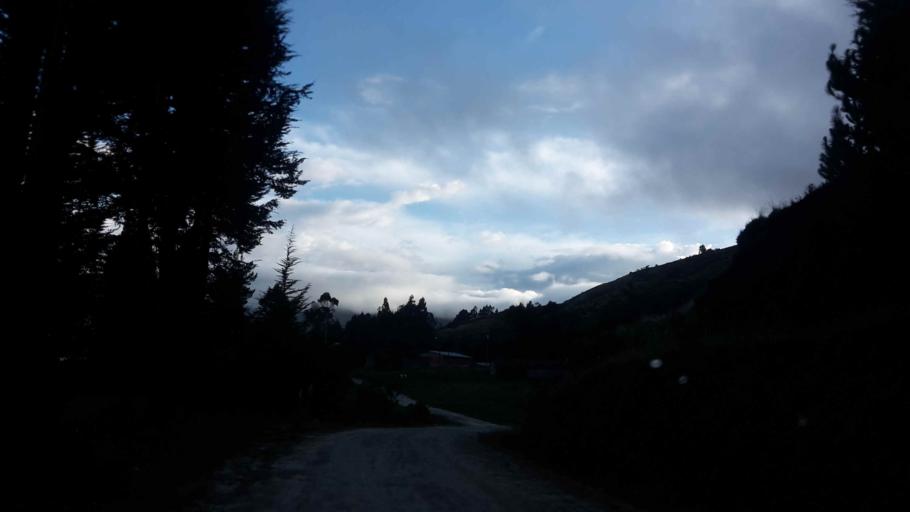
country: BO
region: Cochabamba
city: Colomi
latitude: -17.2596
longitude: -65.9059
